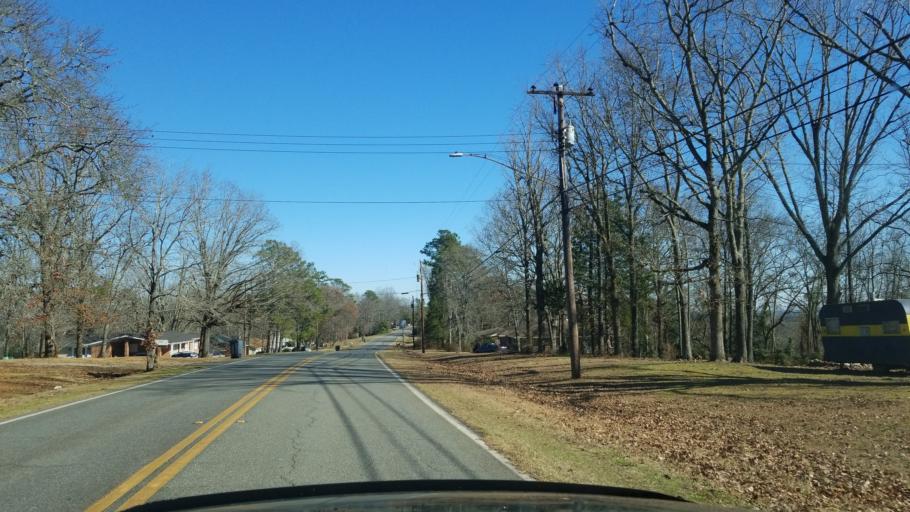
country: US
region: Georgia
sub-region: Meriwether County
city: Manchester
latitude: 32.8437
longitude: -84.6384
